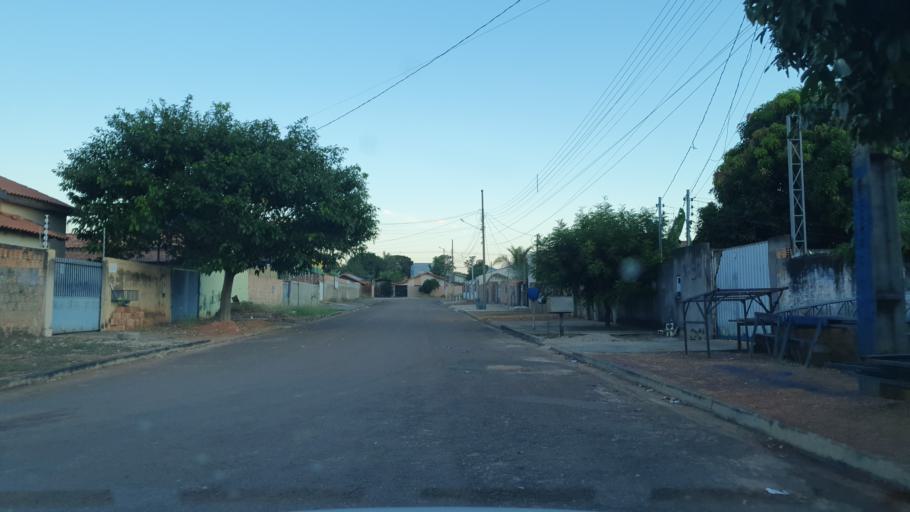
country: BR
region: Mato Grosso
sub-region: Pontes E Lacerda
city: Pontes e Lacerda
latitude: -15.2244
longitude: -59.3249
